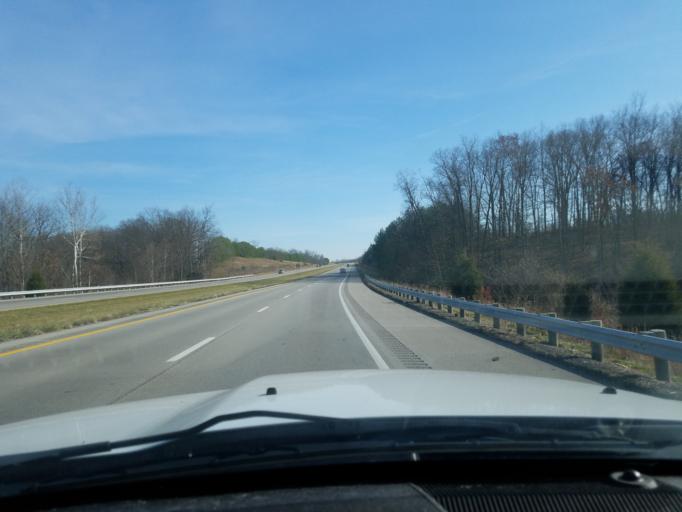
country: US
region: Ohio
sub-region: Pike County
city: Piketon
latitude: 39.0536
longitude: -82.9604
